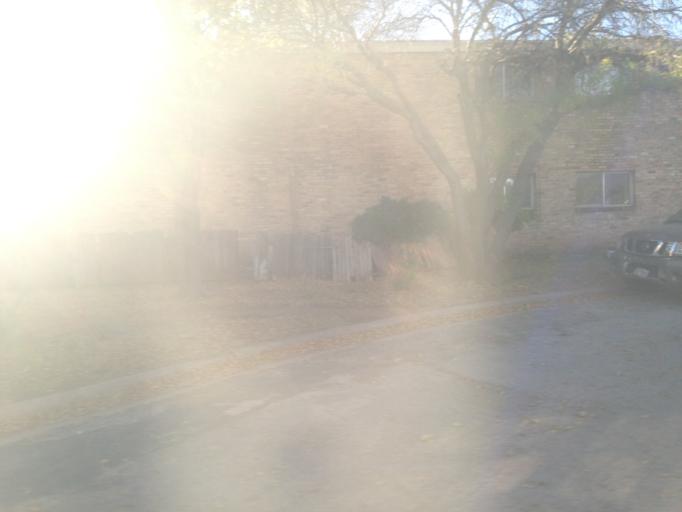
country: US
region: Texas
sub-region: Taylor County
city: Abilene
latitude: 32.4534
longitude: -99.7580
